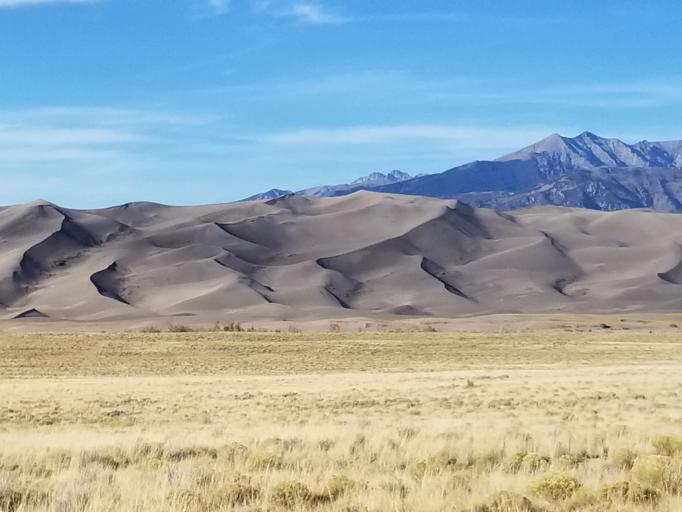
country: US
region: Colorado
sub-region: Alamosa County
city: Alamosa East
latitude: 37.7149
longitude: -105.5271
